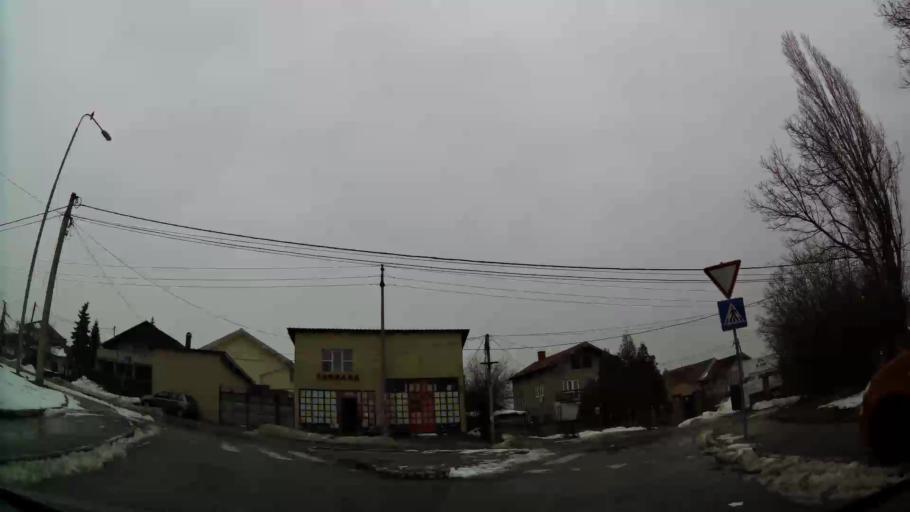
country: RS
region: Central Serbia
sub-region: Belgrade
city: Vozdovac
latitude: 44.7499
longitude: 20.4945
